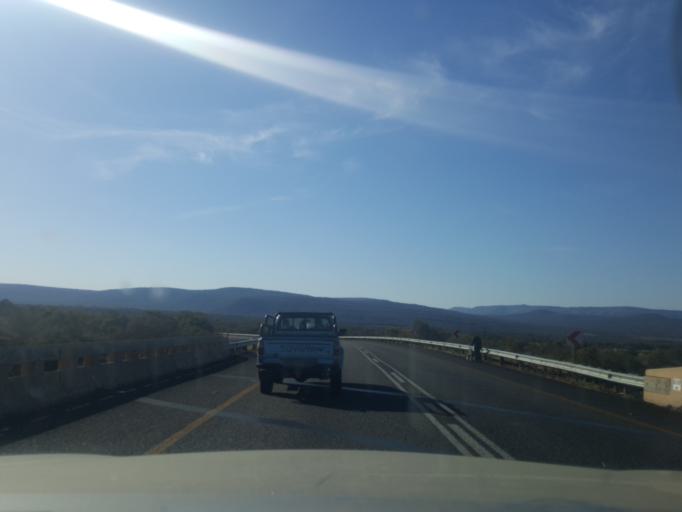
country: ZA
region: North-West
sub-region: Ngaka Modiri Molema District Municipality
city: Zeerust
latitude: -25.5311
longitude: 26.1909
